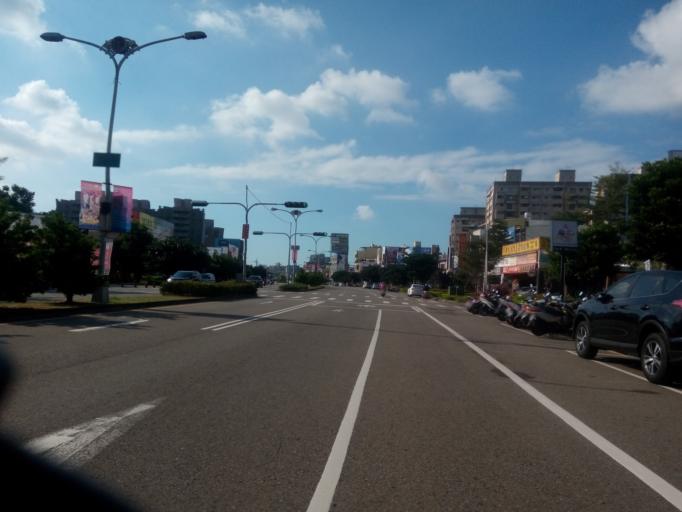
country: TW
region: Taiwan
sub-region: Hsinchu
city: Hsinchu
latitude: 24.6925
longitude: 120.9014
